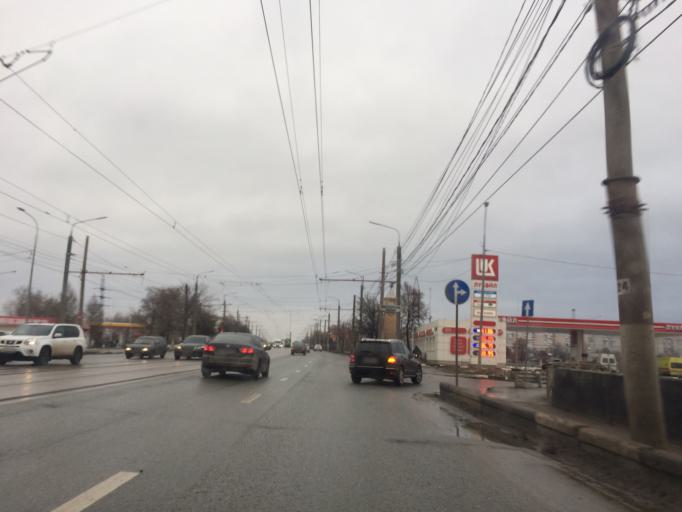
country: RU
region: Tula
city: Tula
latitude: 54.1941
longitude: 37.6309
